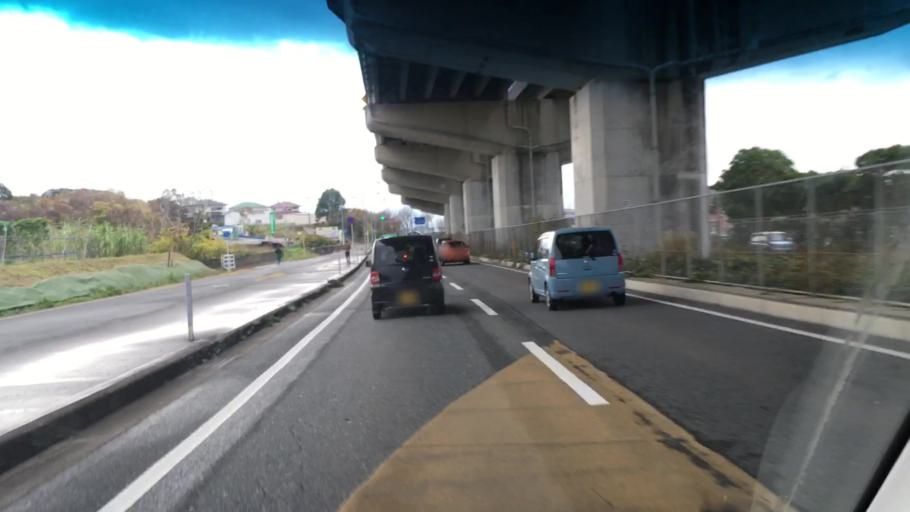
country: JP
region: Fukuoka
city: Maebaru-chuo
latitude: 33.5691
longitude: 130.2485
